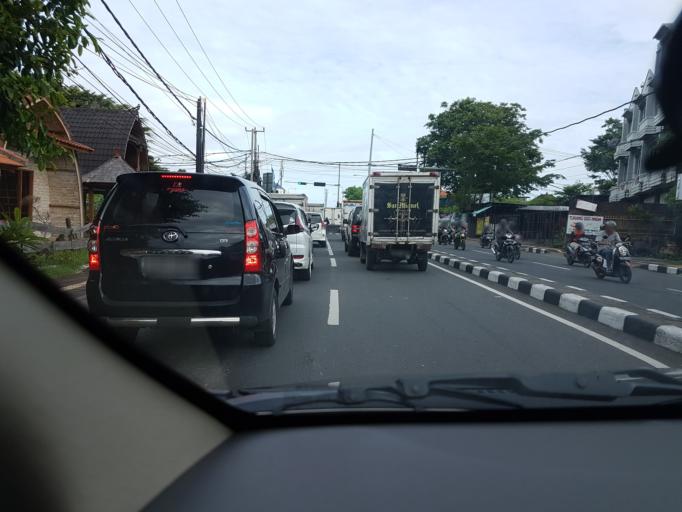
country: ID
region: Bali
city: Denpasar
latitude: -8.6690
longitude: 115.1908
